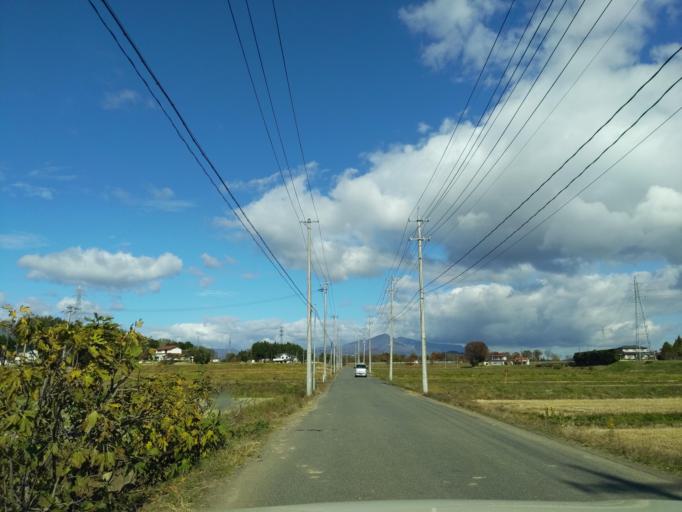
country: JP
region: Fukushima
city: Koriyama
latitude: 37.4436
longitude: 140.3254
